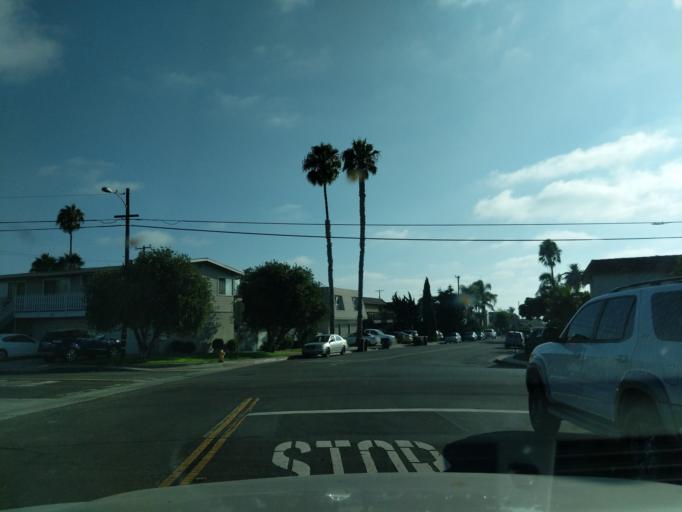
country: US
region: California
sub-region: Orange County
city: San Clemente
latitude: 33.4268
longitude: -117.6208
